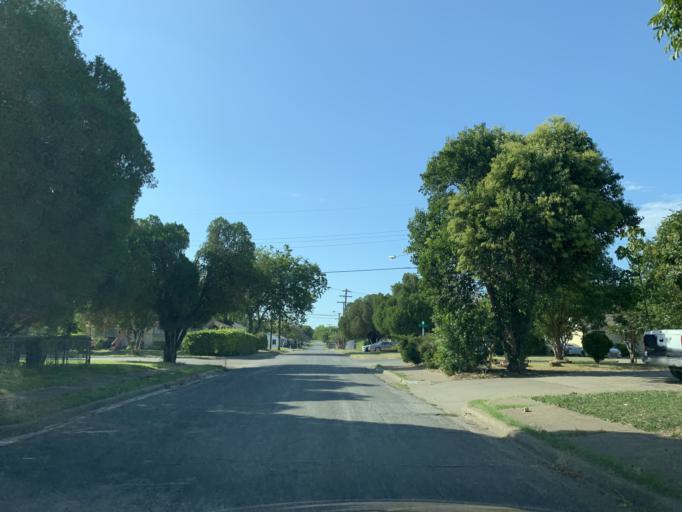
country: US
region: Texas
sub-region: Dallas County
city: Dallas
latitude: 32.7058
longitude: -96.7932
